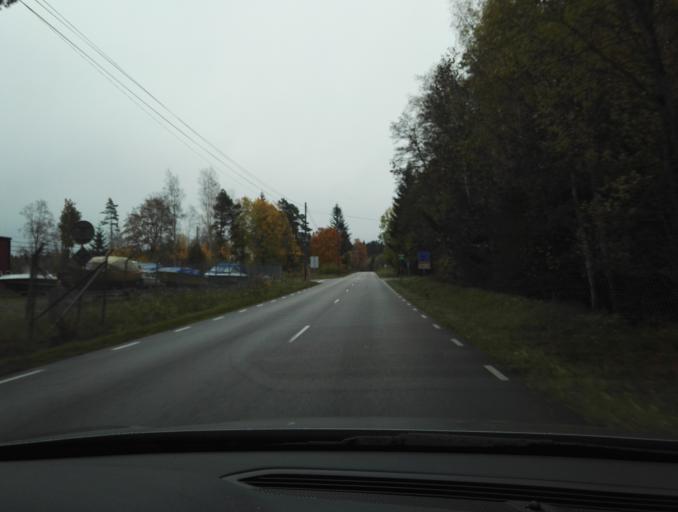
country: SE
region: Kronoberg
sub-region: Vaxjo Kommun
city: Rottne
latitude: 57.0301
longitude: 14.8157
